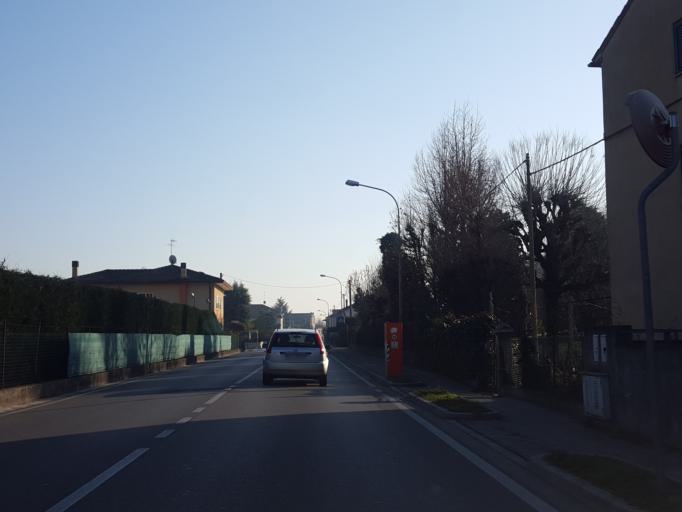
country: IT
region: Veneto
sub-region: Provincia di Vicenza
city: Torri di Quartesolo
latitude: 45.5212
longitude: 11.6371
